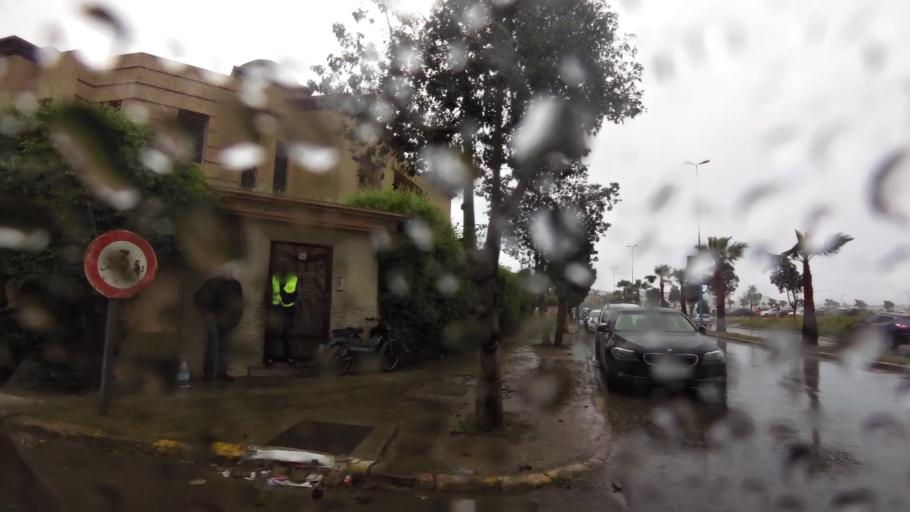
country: MA
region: Grand Casablanca
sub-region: Casablanca
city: Casablanca
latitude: 33.5451
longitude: -7.6675
